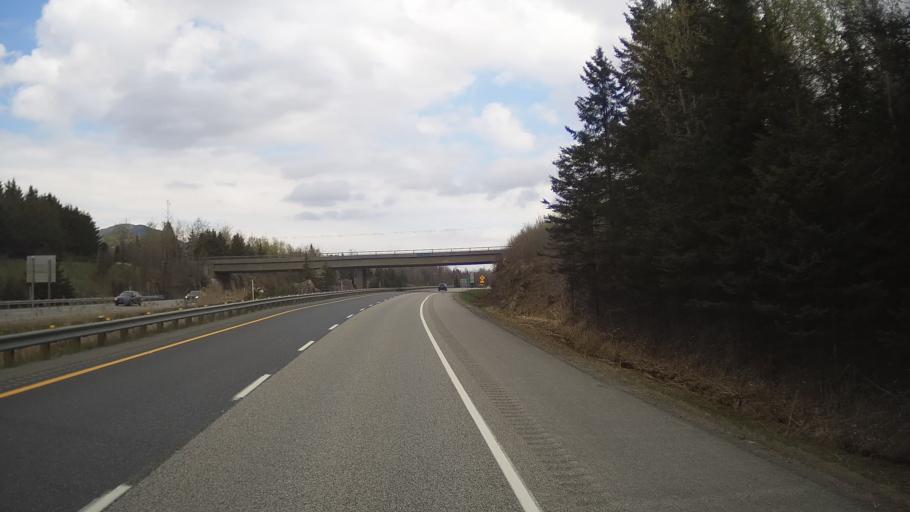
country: CA
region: Quebec
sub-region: Estrie
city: Magog
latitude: 45.2976
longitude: -72.3073
